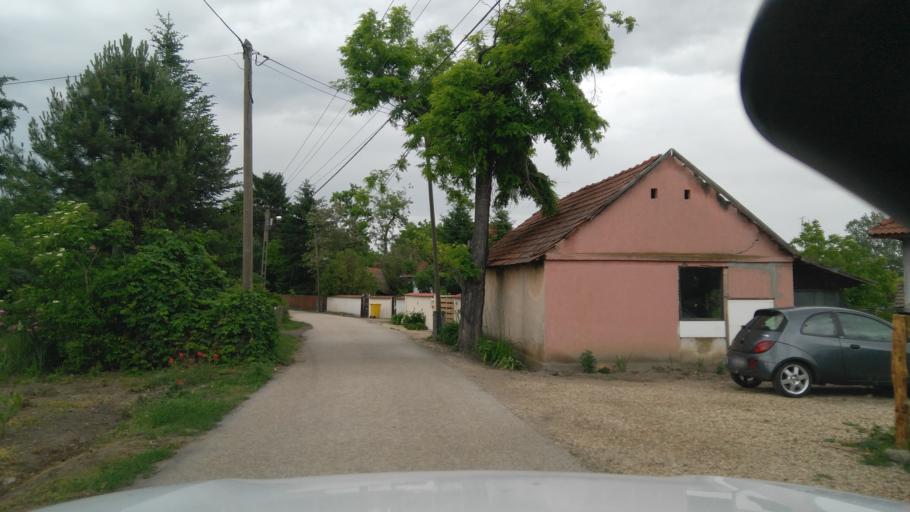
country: HU
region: Bekes
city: Bekescsaba
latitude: 46.6668
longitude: 21.1768
